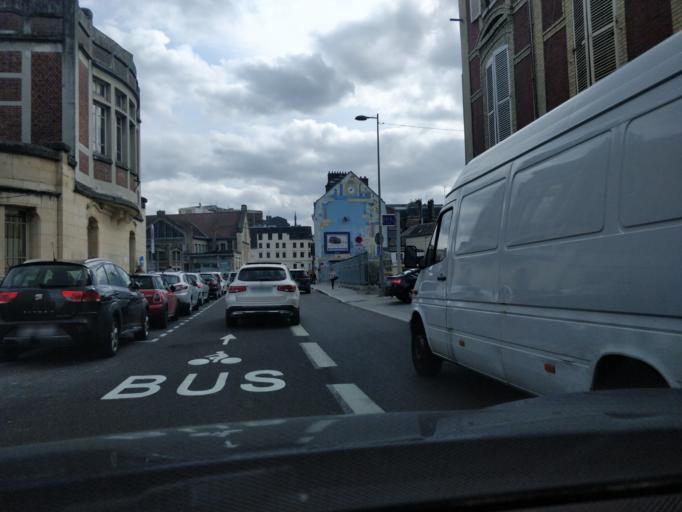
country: FR
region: Haute-Normandie
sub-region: Departement de la Seine-Maritime
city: Rouen
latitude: 49.4499
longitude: 1.0930
